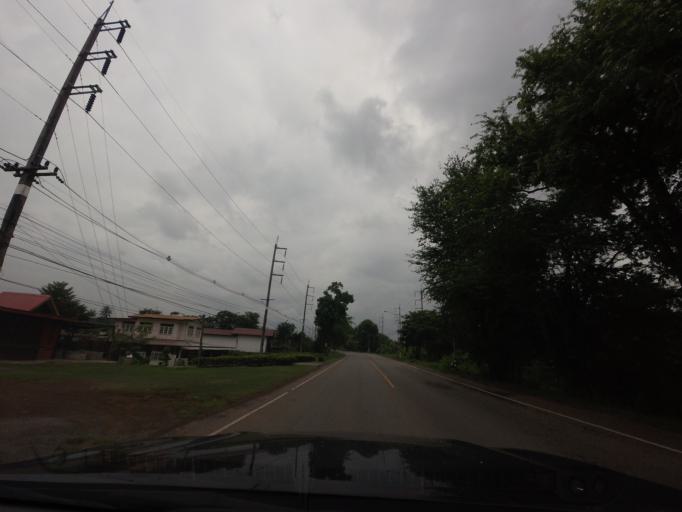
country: TH
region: Nong Khai
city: Si Chiang Mai
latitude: 17.9054
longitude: 102.6071
